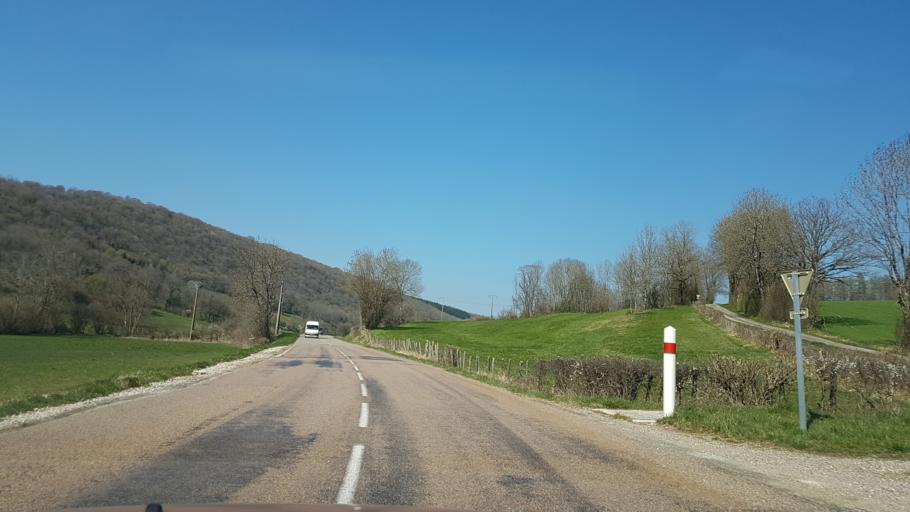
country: FR
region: Franche-Comte
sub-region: Departement du Jura
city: Orgelet
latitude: 46.5462
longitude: 5.6553
